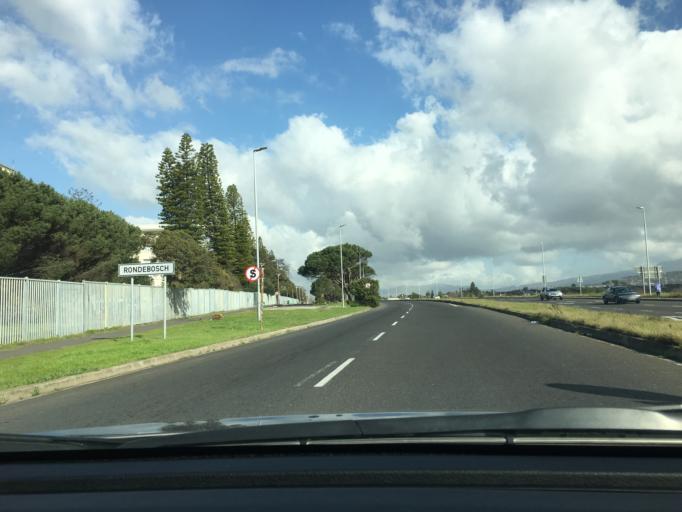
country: ZA
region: Western Cape
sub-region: City of Cape Town
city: Rosebank
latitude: -33.9526
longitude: 18.4863
